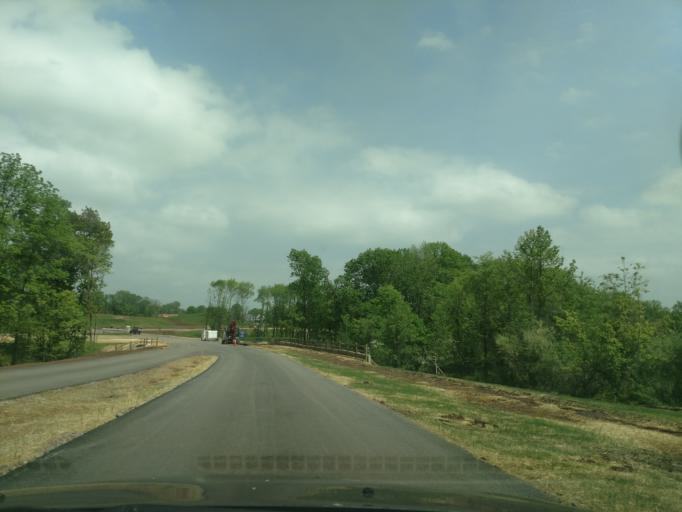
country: US
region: Pennsylvania
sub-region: Chester County
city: Spring City
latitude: 40.1439
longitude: -75.5462
